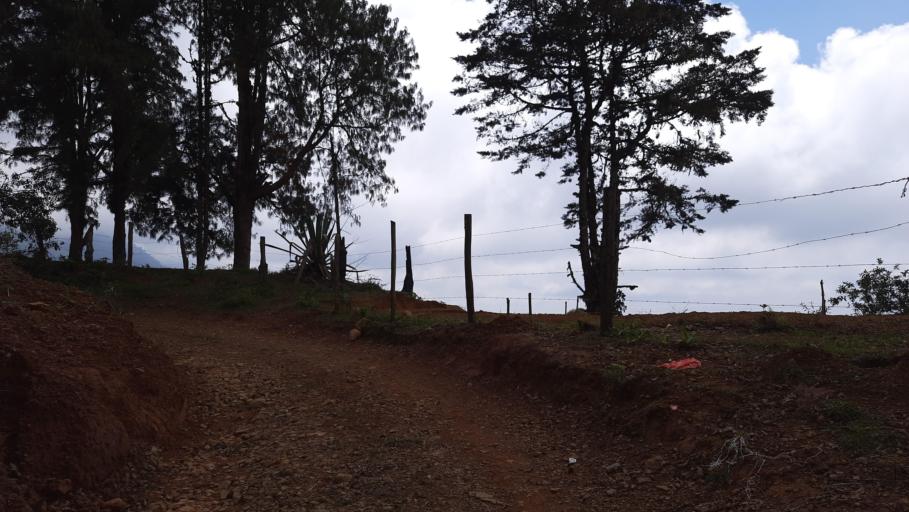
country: CO
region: Cauca
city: Buenos Aires
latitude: 3.1800
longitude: -76.7234
